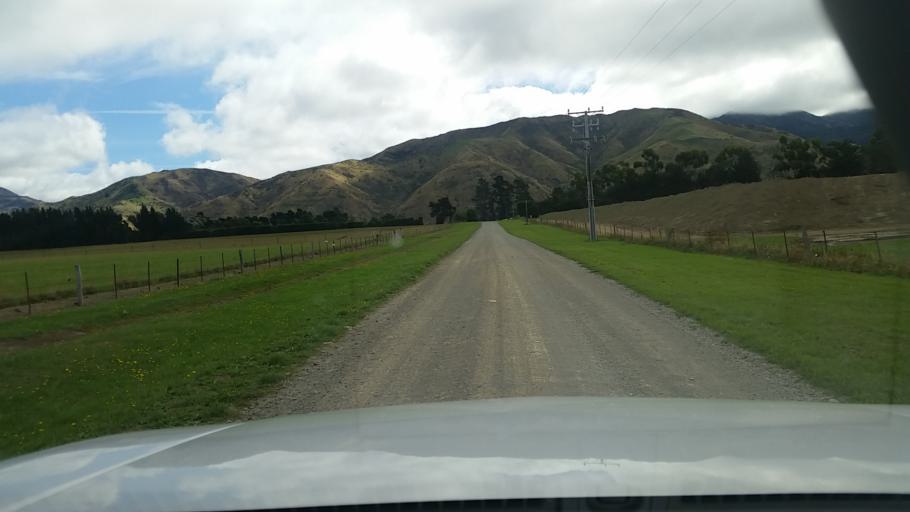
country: NZ
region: Marlborough
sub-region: Marlborough District
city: Blenheim
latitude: -41.6984
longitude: 173.9526
